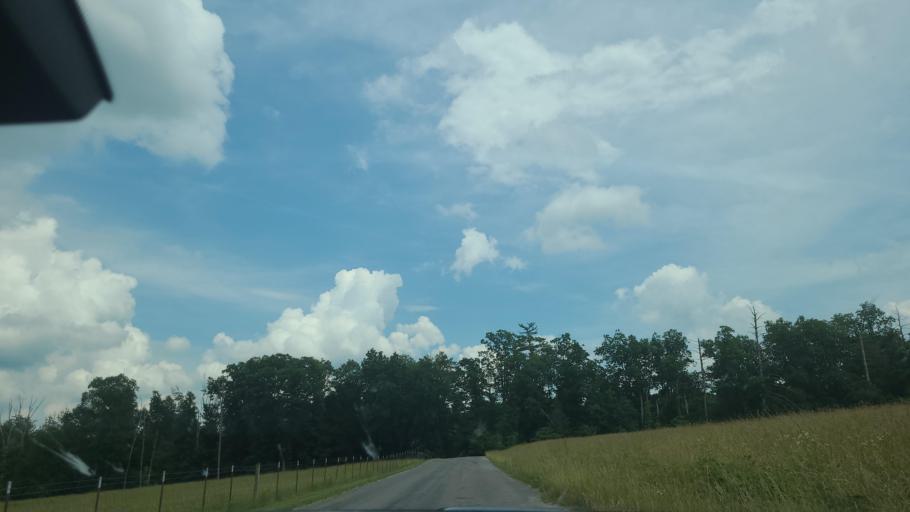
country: US
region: Tennessee
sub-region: Cumberland County
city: Lake Tansi
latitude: 35.7703
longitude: -85.0558
